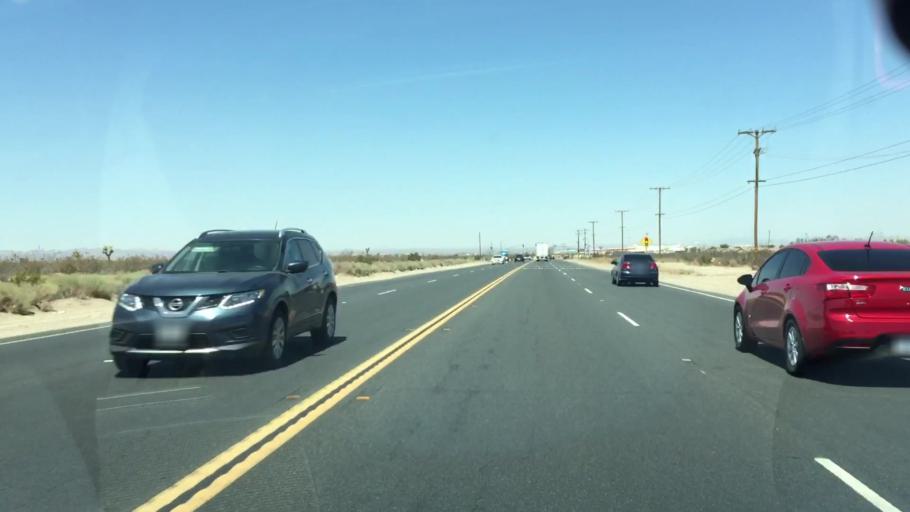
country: US
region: California
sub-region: San Bernardino County
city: Mountain View Acres
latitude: 34.4663
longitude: -117.3995
